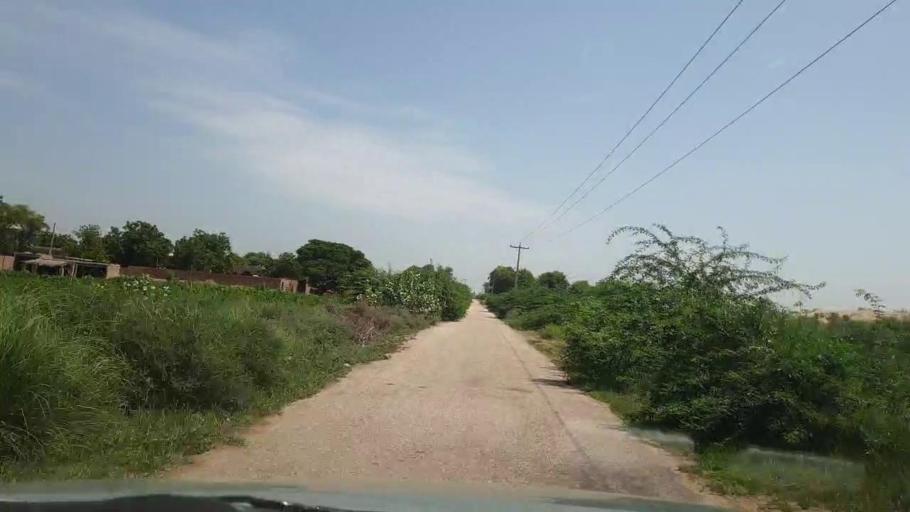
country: PK
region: Sindh
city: Bozdar
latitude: 27.1127
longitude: 68.9867
